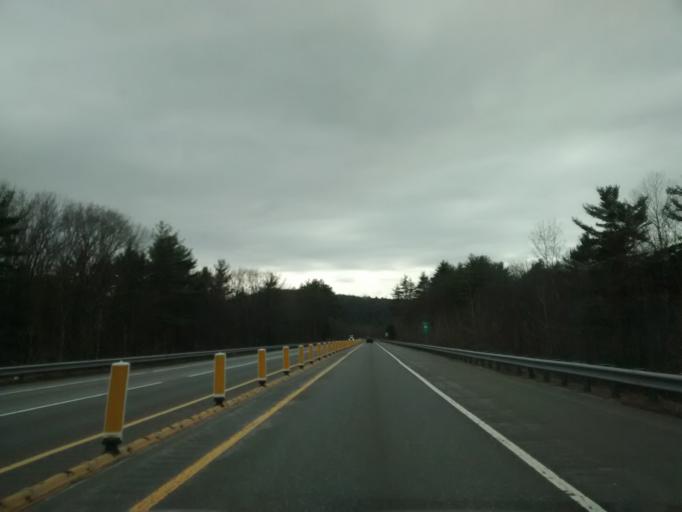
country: US
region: Massachusetts
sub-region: Worcester County
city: Athol
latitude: 42.5636
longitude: -72.2408
